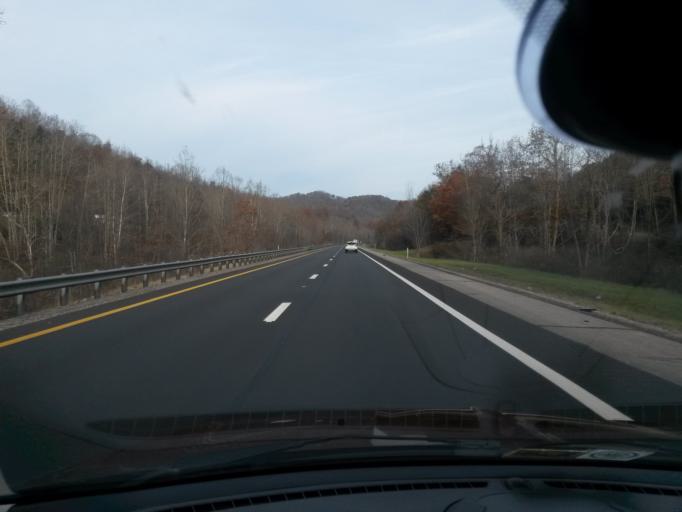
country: US
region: West Virginia
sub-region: Raleigh County
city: Prosperity
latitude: 37.8589
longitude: -81.2555
